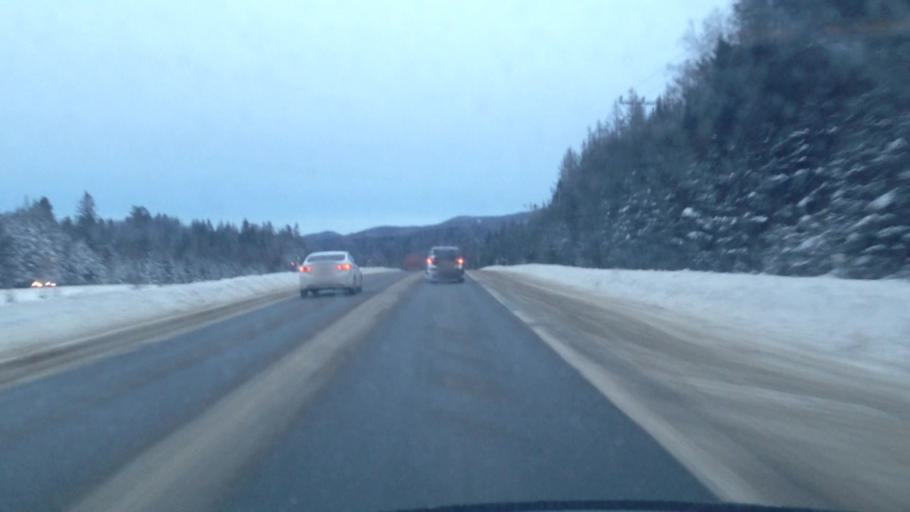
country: CA
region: Quebec
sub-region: Laurentides
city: Mont-Tremblant
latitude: 46.1123
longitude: -74.5356
